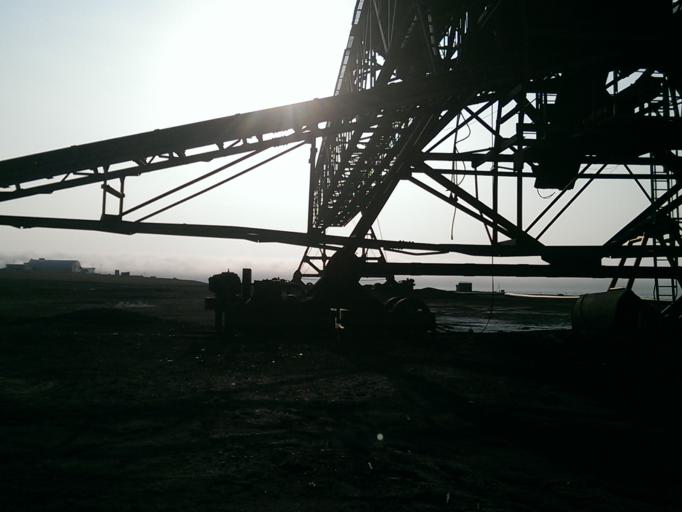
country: SJ
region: Svalbard
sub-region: Spitsbergen
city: Longyearbyen
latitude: 78.2468
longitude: 15.5450
